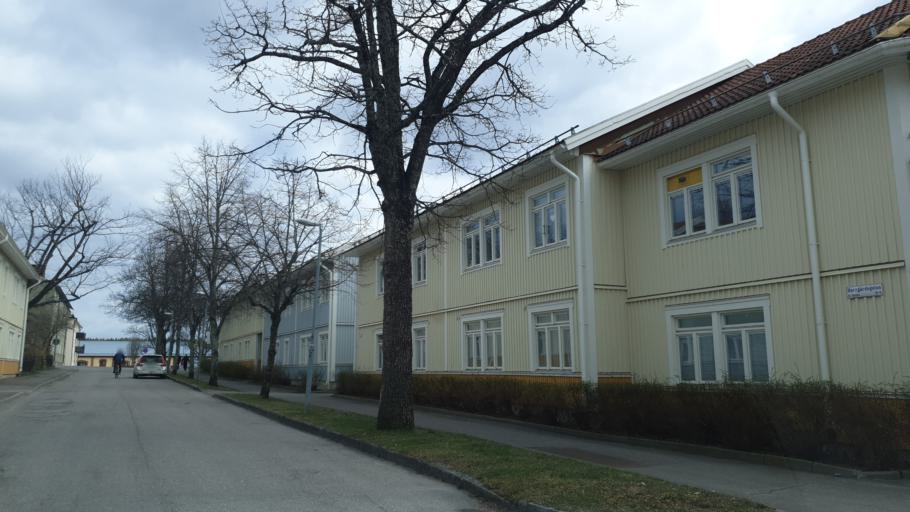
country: SE
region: OErebro
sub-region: Nora Kommun
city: Nora
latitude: 59.5169
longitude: 15.0379
